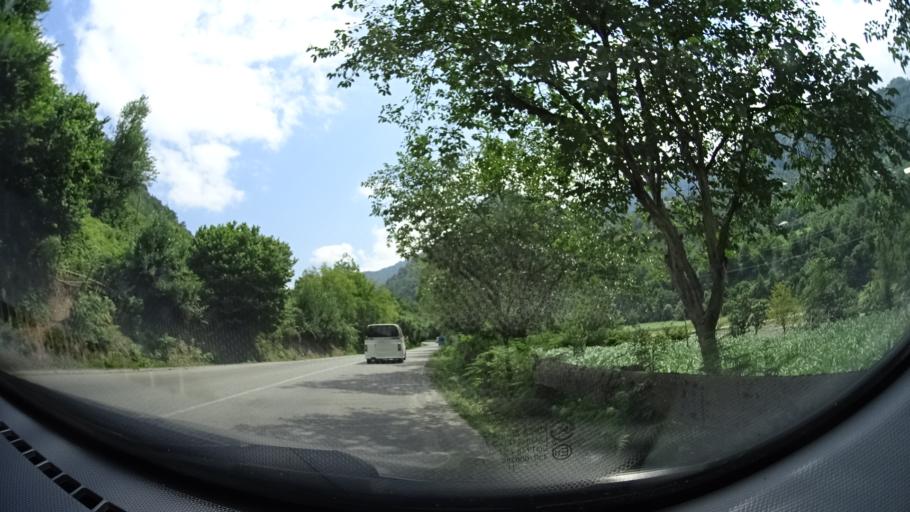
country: TR
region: Artvin
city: Camili
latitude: 41.5665
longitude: 41.8354
